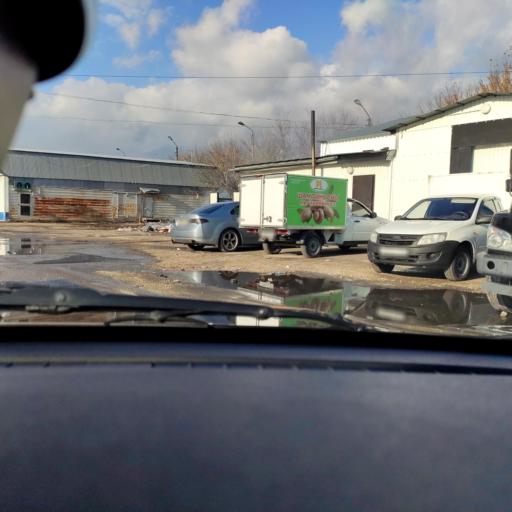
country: RU
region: Samara
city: Zhigulevsk
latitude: 53.5208
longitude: 49.4795
